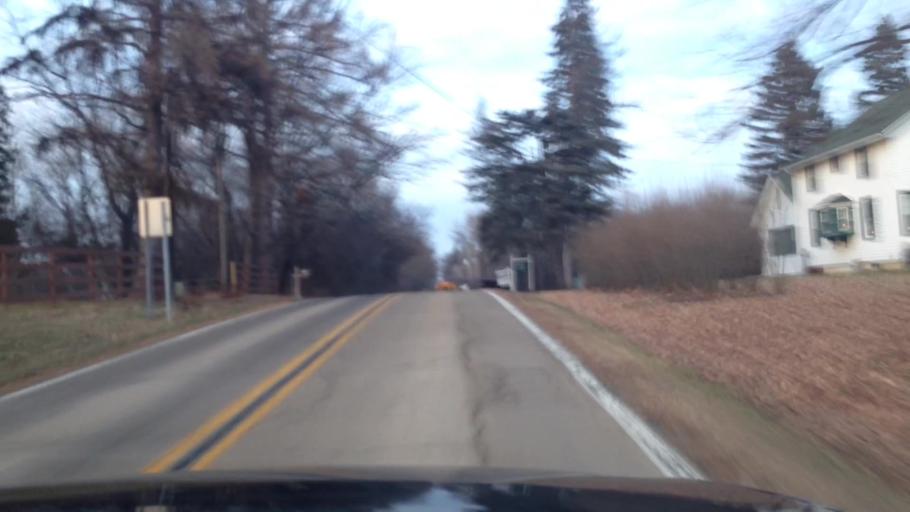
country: US
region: Illinois
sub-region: Cook County
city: Barrington Hills
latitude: 42.1061
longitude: -88.1947
